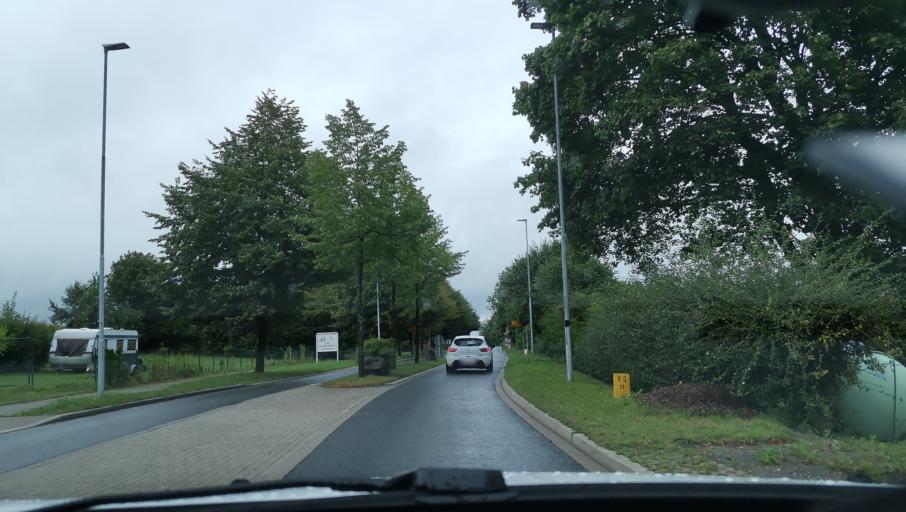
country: DE
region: North Rhine-Westphalia
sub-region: Regierungsbezirk Arnsberg
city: Breckerfeld
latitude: 51.3016
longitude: 7.4617
